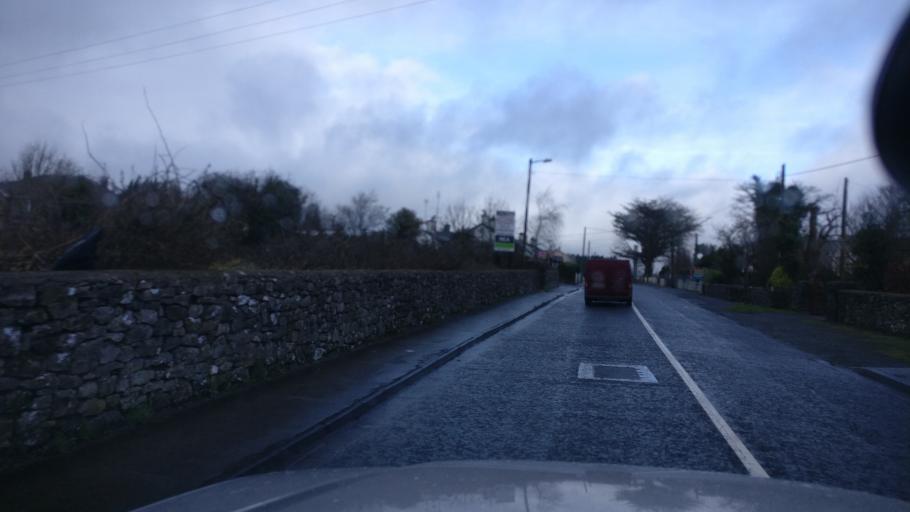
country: IE
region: Connaught
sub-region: County Galway
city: Loughrea
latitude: 53.2043
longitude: -8.5713
